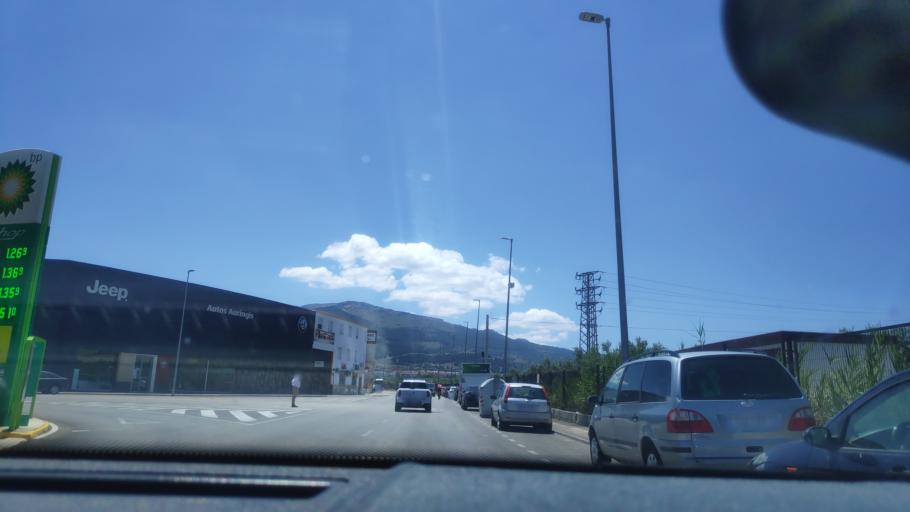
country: ES
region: Andalusia
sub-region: Provincia de Jaen
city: Jaen
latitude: 37.7999
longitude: -3.7910
